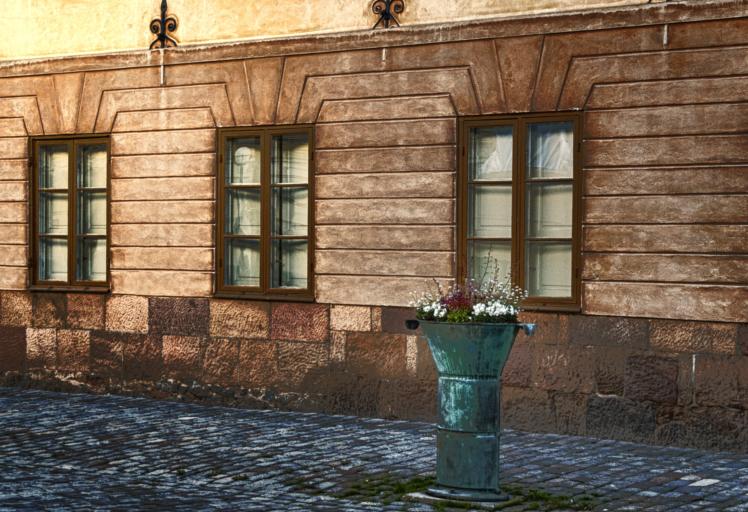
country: SE
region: Stockholm
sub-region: Stockholms Kommun
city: Stockholm
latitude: 59.3307
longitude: 18.0752
